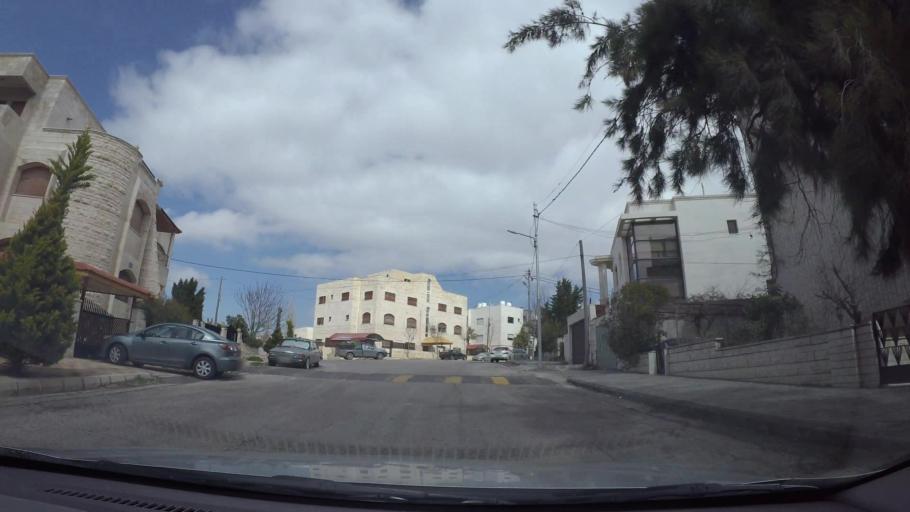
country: JO
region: Amman
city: Al Jubayhah
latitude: 31.9939
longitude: 35.8526
